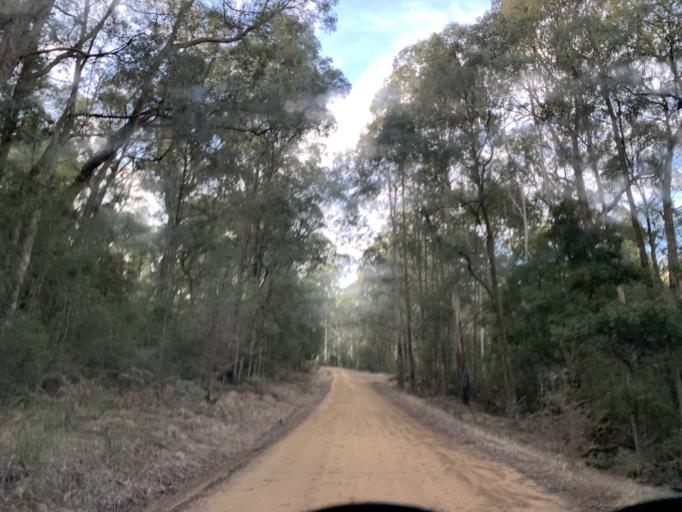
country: AU
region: Victoria
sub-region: Mansfield
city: Mansfield
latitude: -36.8896
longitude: 146.1207
